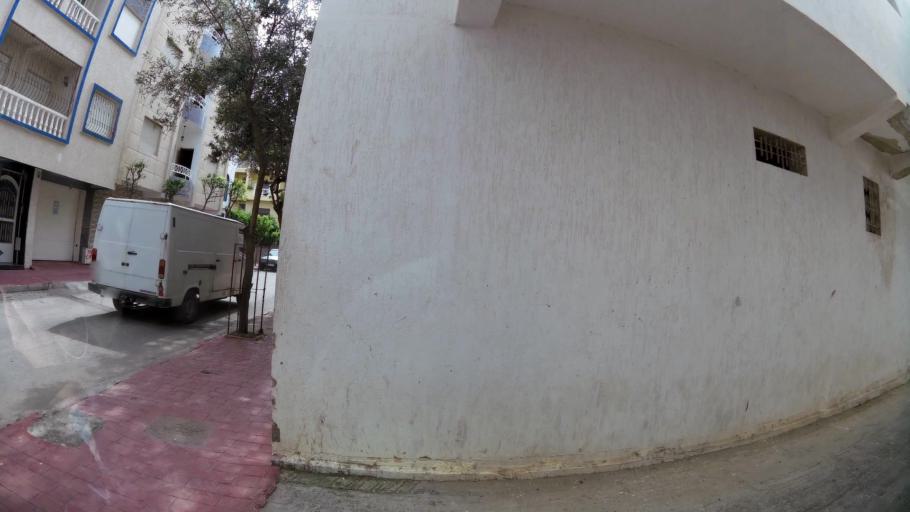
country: MA
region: Tanger-Tetouan
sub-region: Tetouan
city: Martil
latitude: 35.6863
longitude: -5.3278
